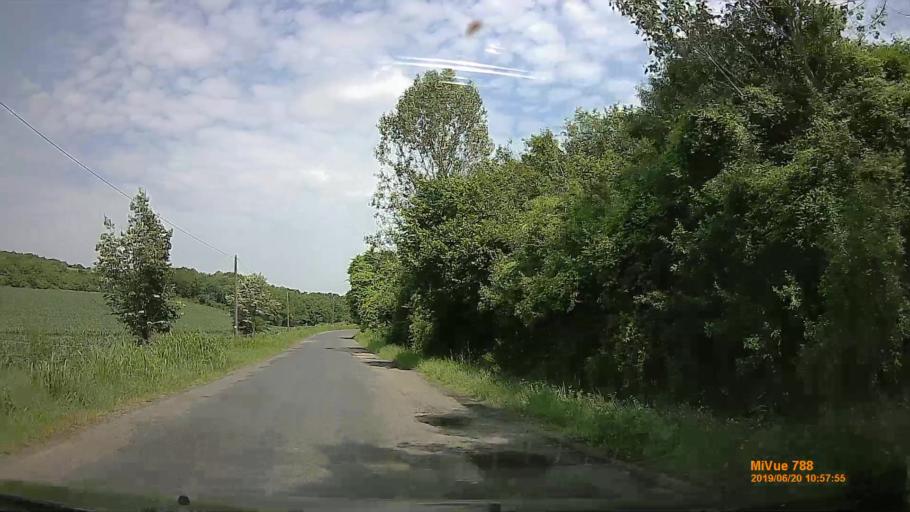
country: HU
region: Baranya
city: Mecseknadasd
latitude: 46.1556
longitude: 18.5186
